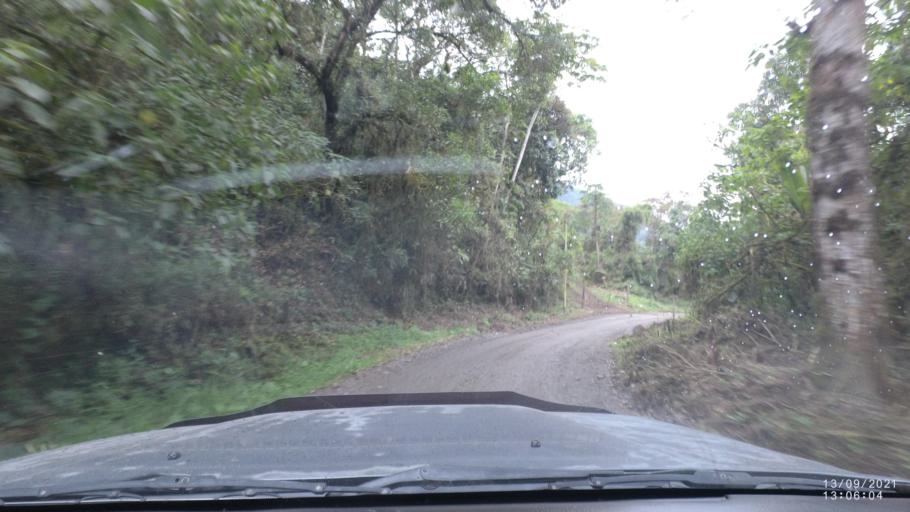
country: BO
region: Cochabamba
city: Colomi
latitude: -17.2227
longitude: -65.8249
